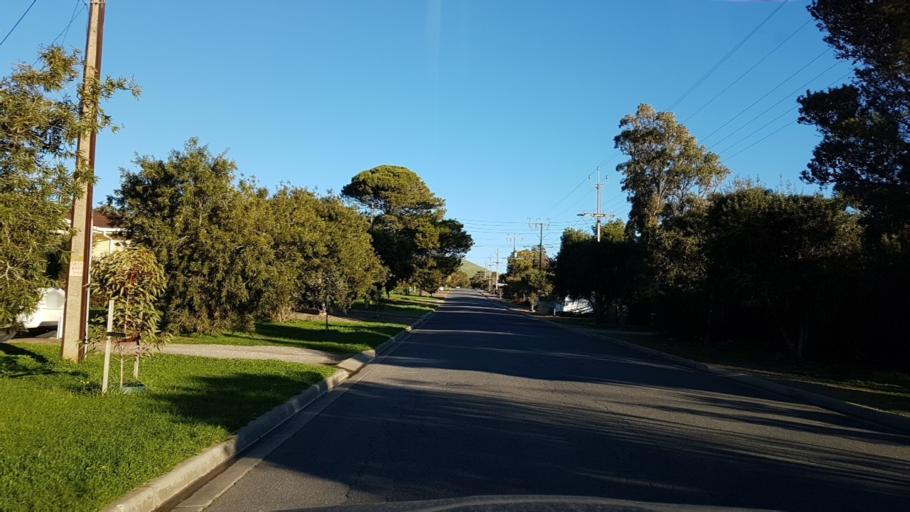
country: AU
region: South Australia
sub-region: Onkaparinga
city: Port Willunga
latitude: -35.3311
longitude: 138.4505
